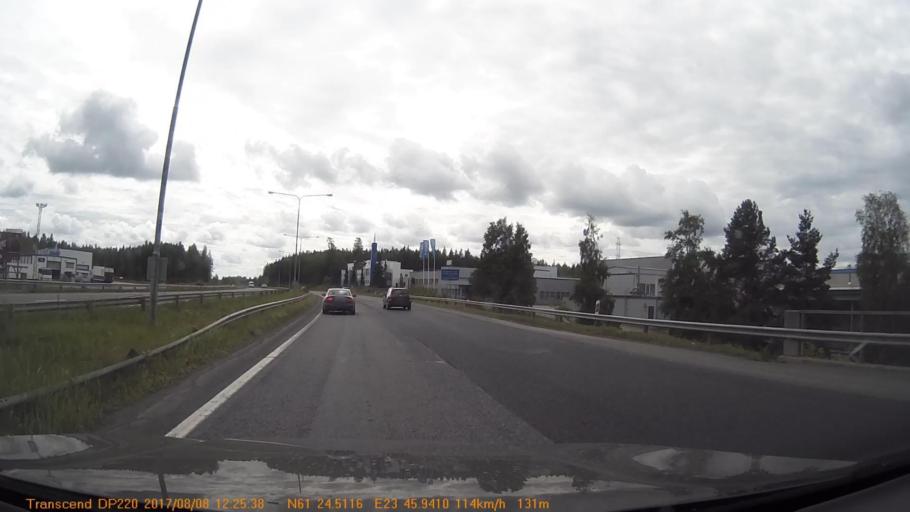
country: FI
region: Pirkanmaa
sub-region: Tampere
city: Lempaeaelae
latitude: 61.4083
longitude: 23.7658
